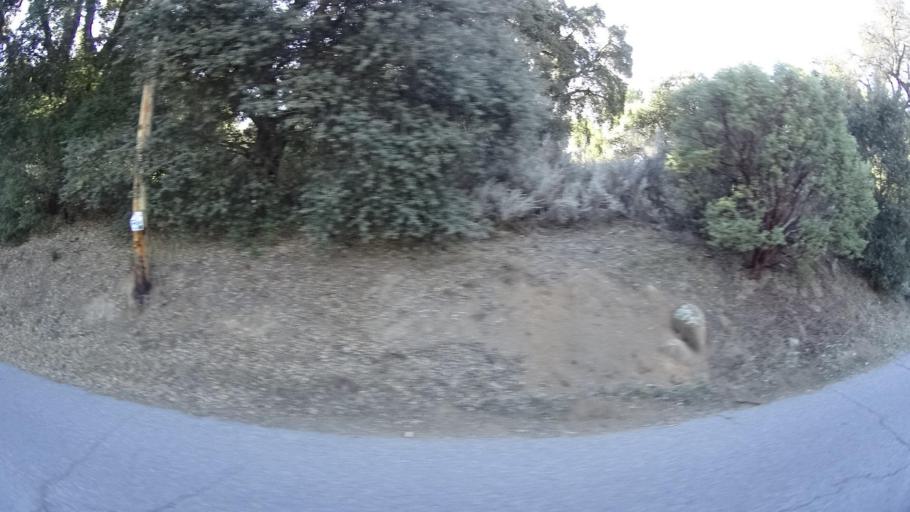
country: US
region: California
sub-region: San Diego County
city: Pine Valley
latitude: 32.8205
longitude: -116.5378
